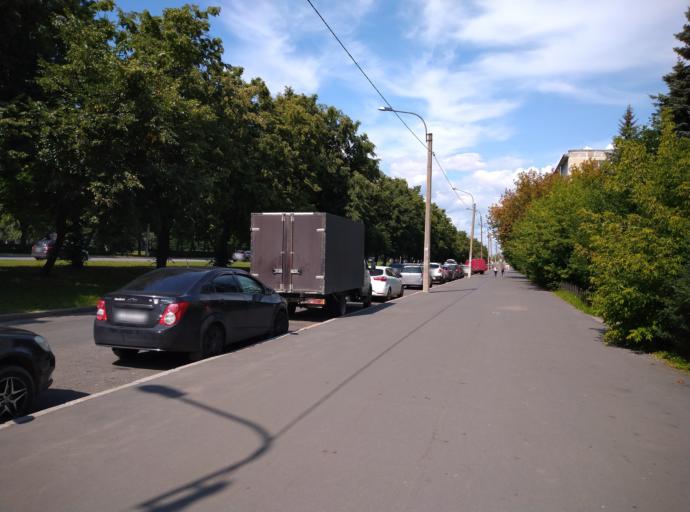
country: RU
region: St.-Petersburg
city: Kupchino
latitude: 59.8595
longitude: 30.3379
